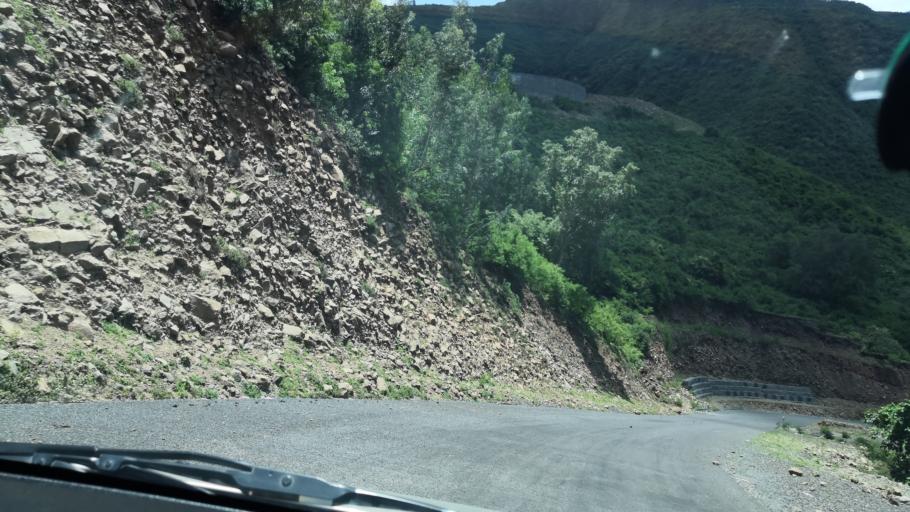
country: ET
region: Amhara
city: Abomsa
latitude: 10.3016
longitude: 39.8898
